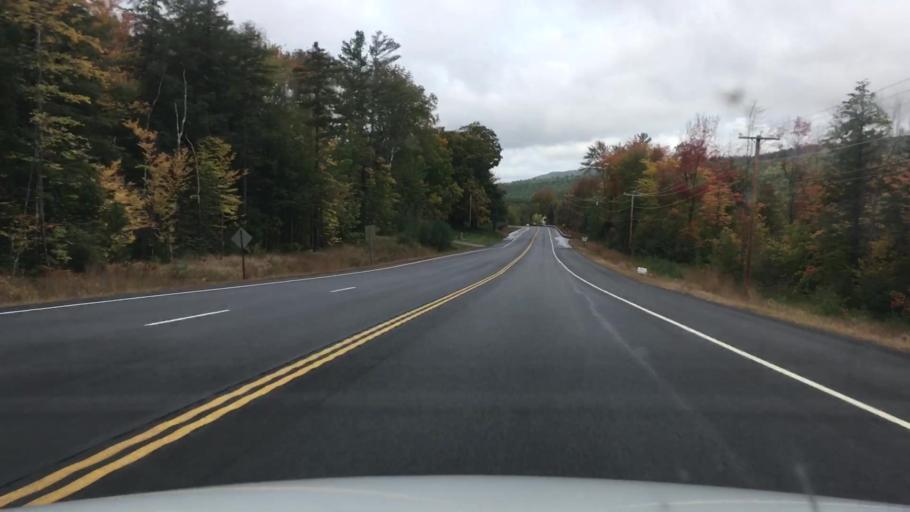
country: US
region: Maine
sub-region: Oxford County
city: Bethel
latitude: 44.4166
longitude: -70.8328
